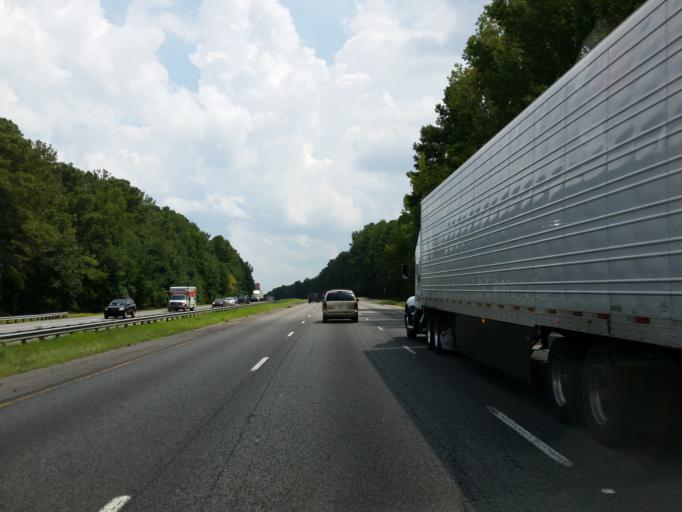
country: US
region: Georgia
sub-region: Henry County
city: Locust Grove
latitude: 33.2343
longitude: -84.0805
